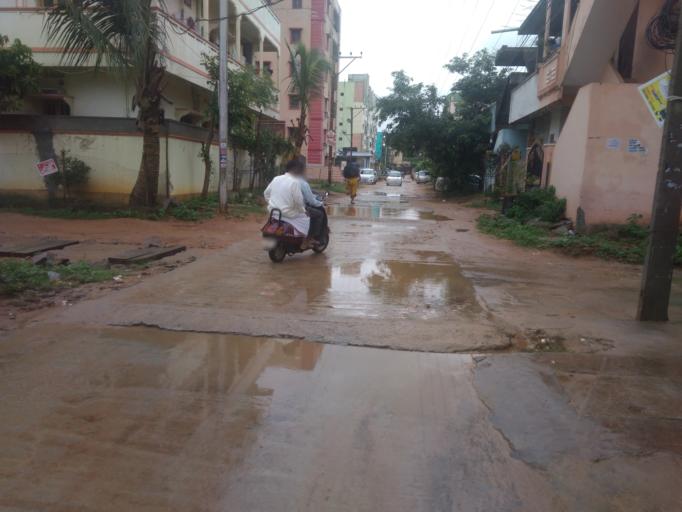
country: IN
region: Telangana
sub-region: Rangareddi
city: Secunderabad
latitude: 17.5123
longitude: 78.5087
